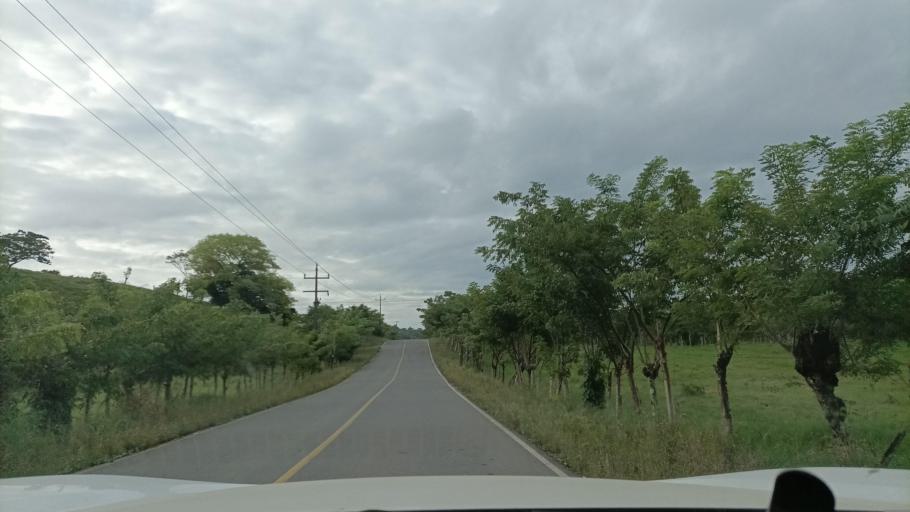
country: MX
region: Veracruz
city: Hidalgotitlan
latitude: 17.6942
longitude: -94.4689
